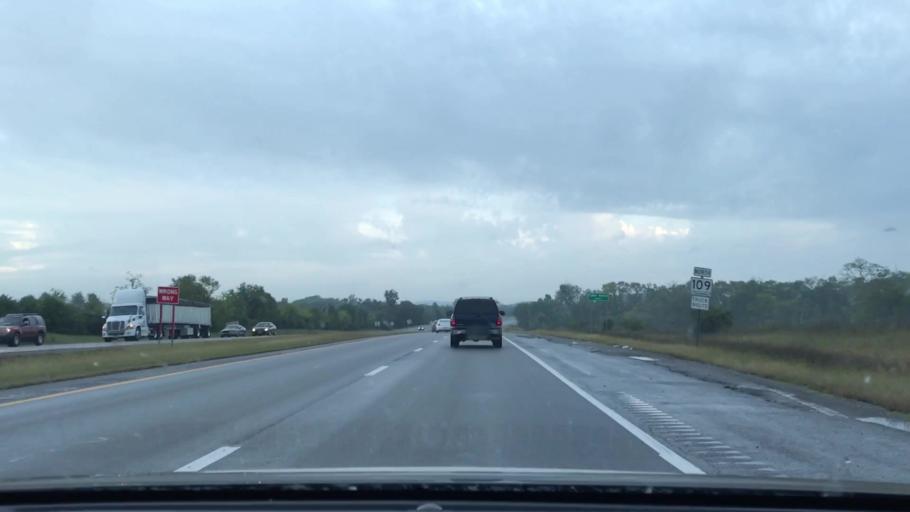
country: US
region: Tennessee
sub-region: Sumner County
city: Gallatin
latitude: 36.3985
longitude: -86.4793
